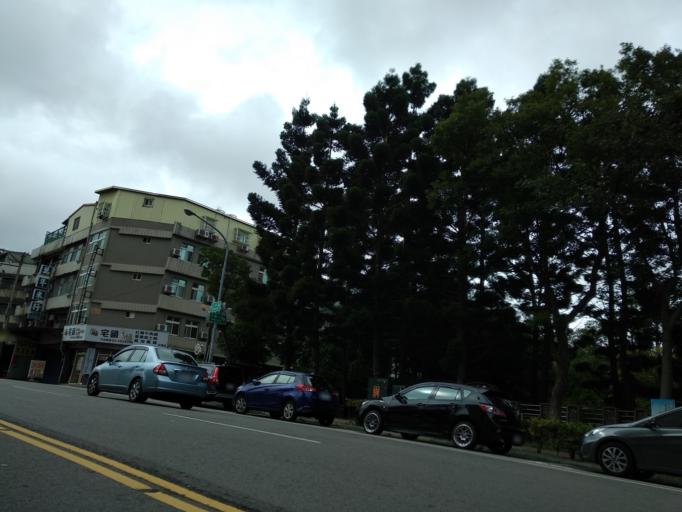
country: TW
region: Taiwan
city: Taoyuan City
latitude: 24.9609
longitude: 121.2106
